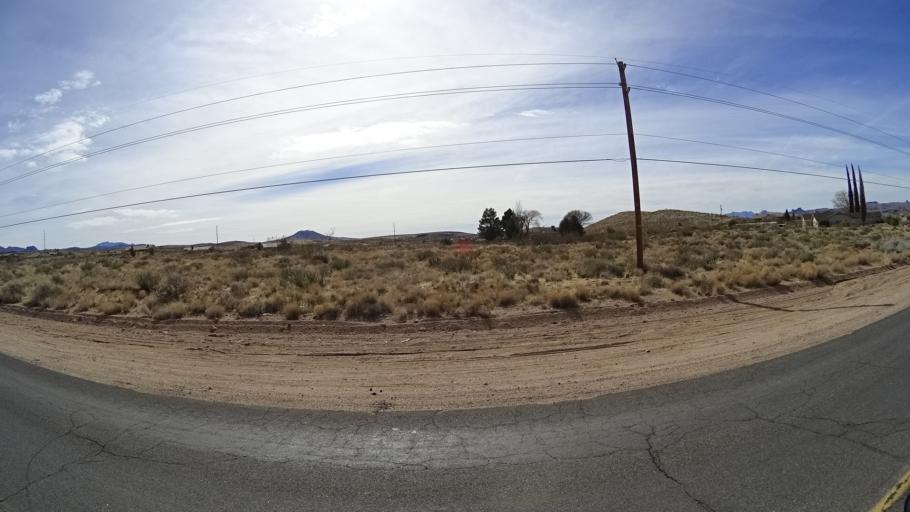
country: US
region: Arizona
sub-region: Mohave County
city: Kingman
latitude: 35.1836
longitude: -114.0014
